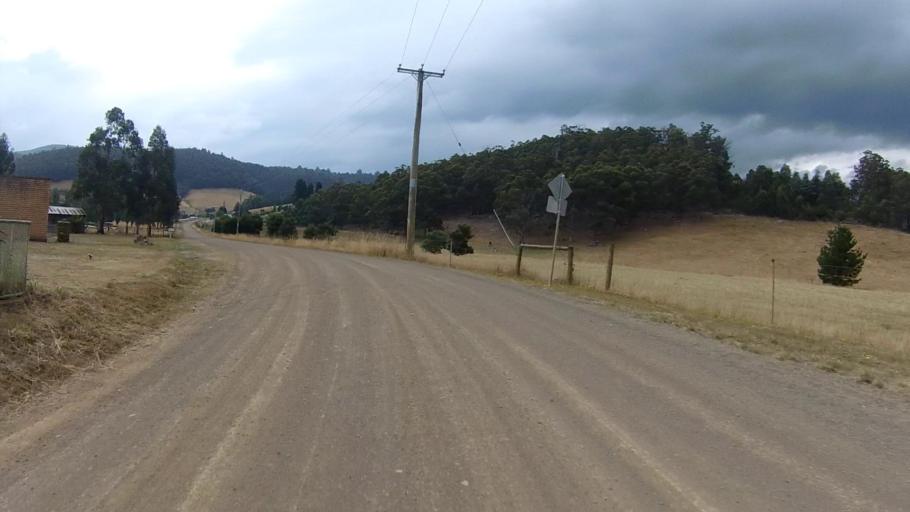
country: AU
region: Tasmania
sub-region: Huon Valley
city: Huonville
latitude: -42.9781
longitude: 147.0551
